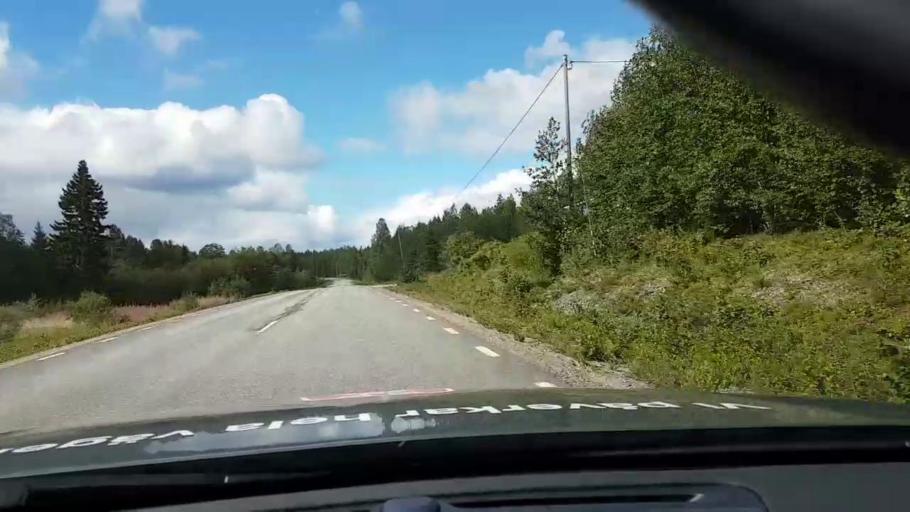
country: SE
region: Vaesternorrland
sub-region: OErnskoeldsviks Kommun
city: Bredbyn
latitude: 63.5284
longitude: 17.9915
